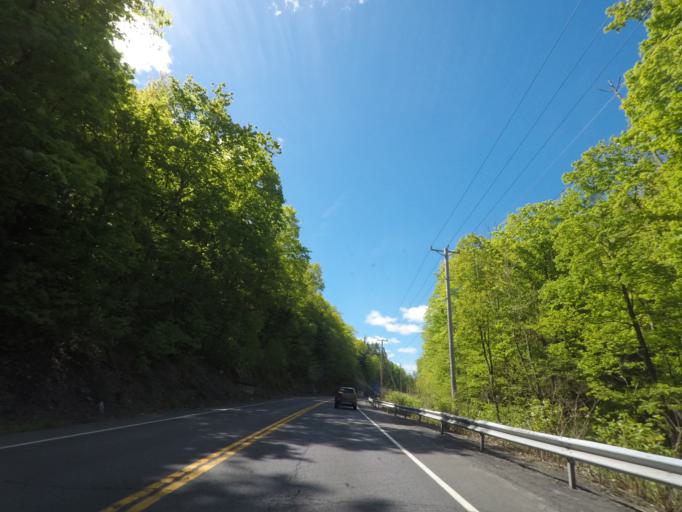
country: US
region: New York
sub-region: Ulster County
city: Lake Katrine
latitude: 42.0202
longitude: -73.9776
